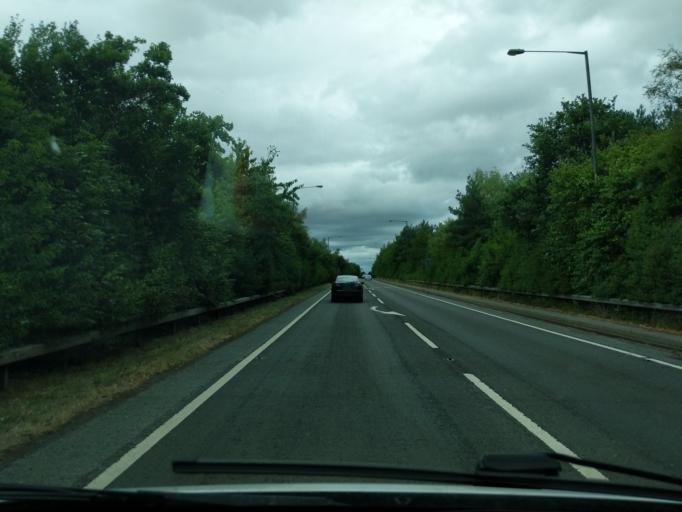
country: GB
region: England
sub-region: Cheshire West and Chester
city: Weaverham
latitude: 53.2562
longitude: -2.5897
